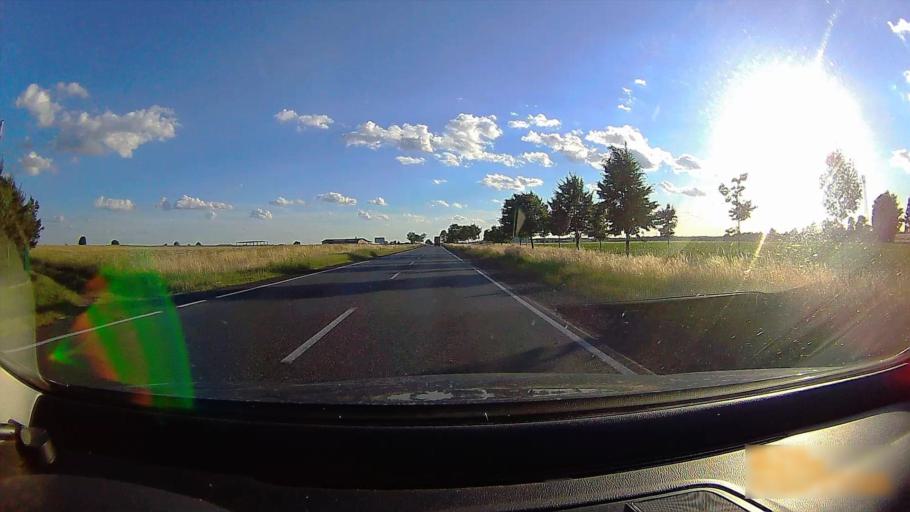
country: PL
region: Greater Poland Voivodeship
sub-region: Powiat ostrowski
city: Skalmierzyce
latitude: 51.6824
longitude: 17.8968
